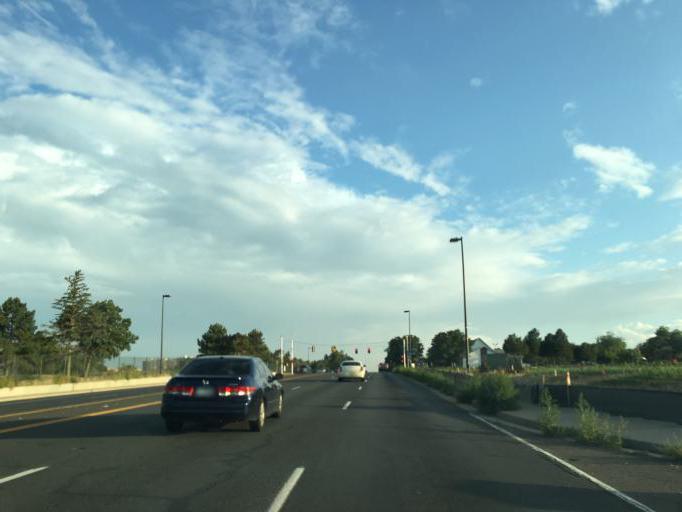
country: US
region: Colorado
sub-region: Adams County
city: Aurora
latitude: 39.7546
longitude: -104.8470
